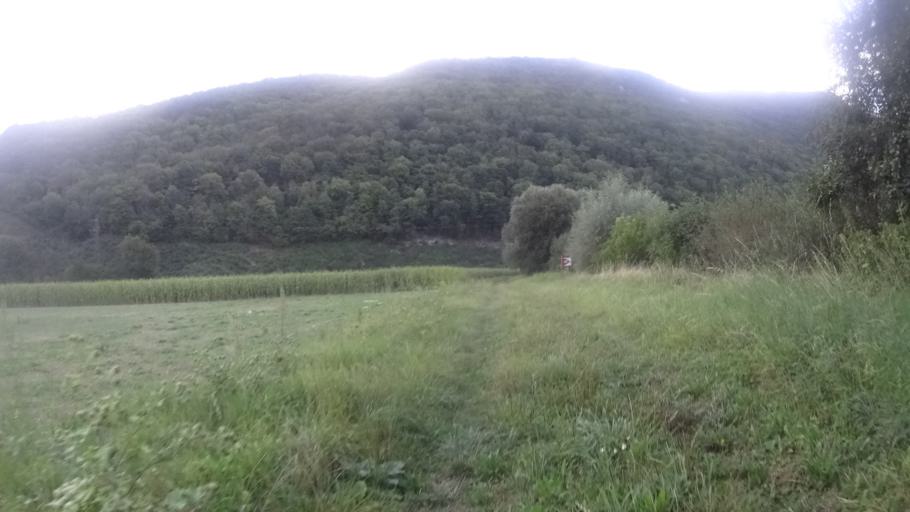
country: FR
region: Franche-Comte
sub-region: Departement du Doubs
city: Montfaucon
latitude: 47.2596
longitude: 6.0823
